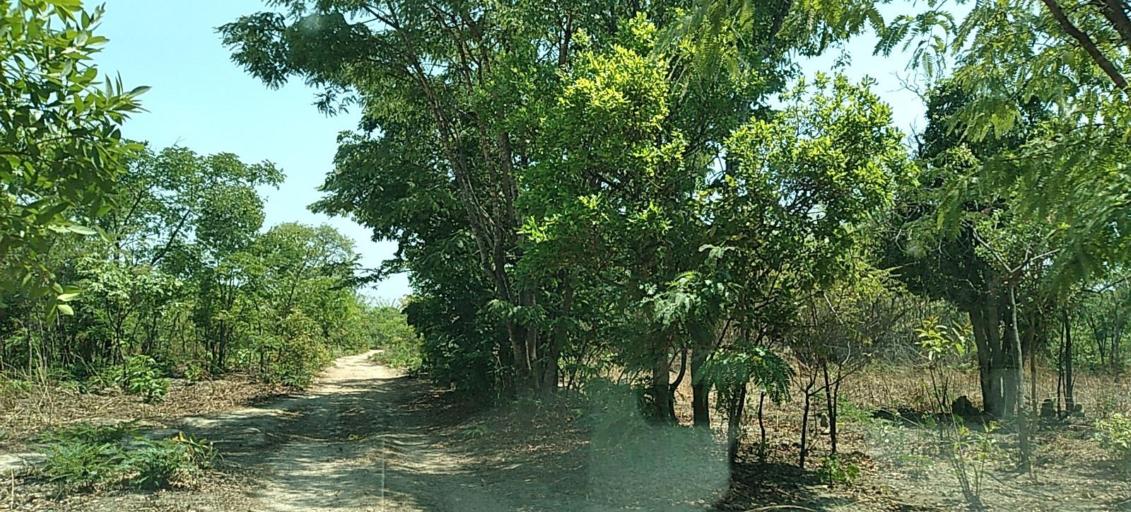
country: ZM
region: Copperbelt
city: Luanshya
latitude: -12.9922
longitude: 28.3279
